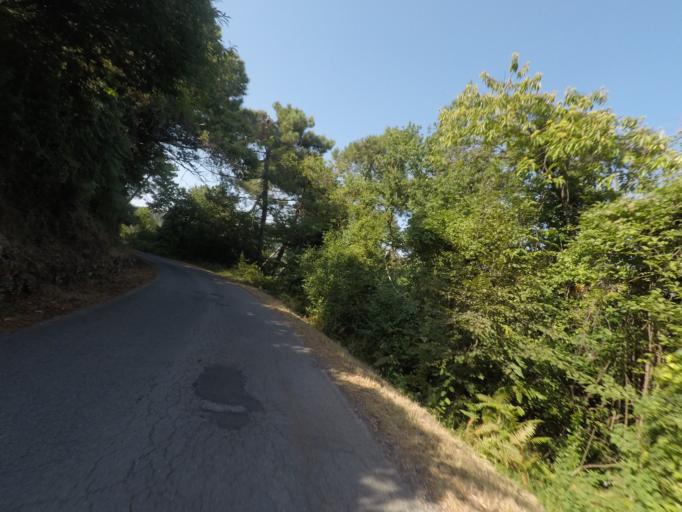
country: IT
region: Tuscany
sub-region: Provincia di Massa-Carrara
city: Carrara
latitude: 44.0792
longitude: 10.0664
